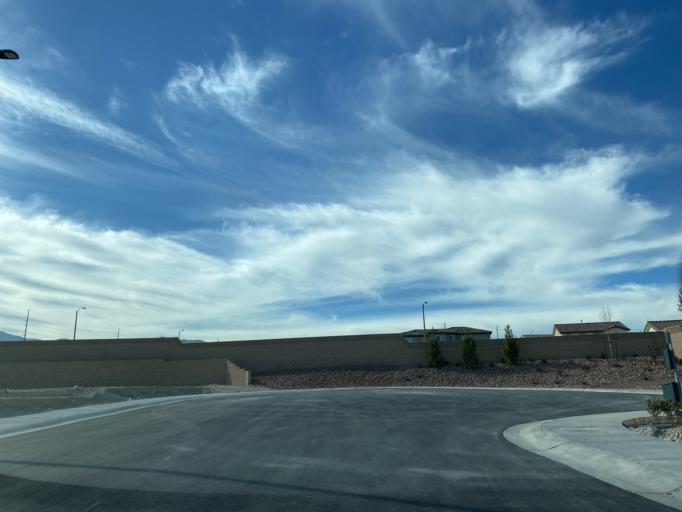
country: US
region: Nevada
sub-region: Clark County
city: Summerlin South
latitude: 36.3082
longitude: -115.3206
